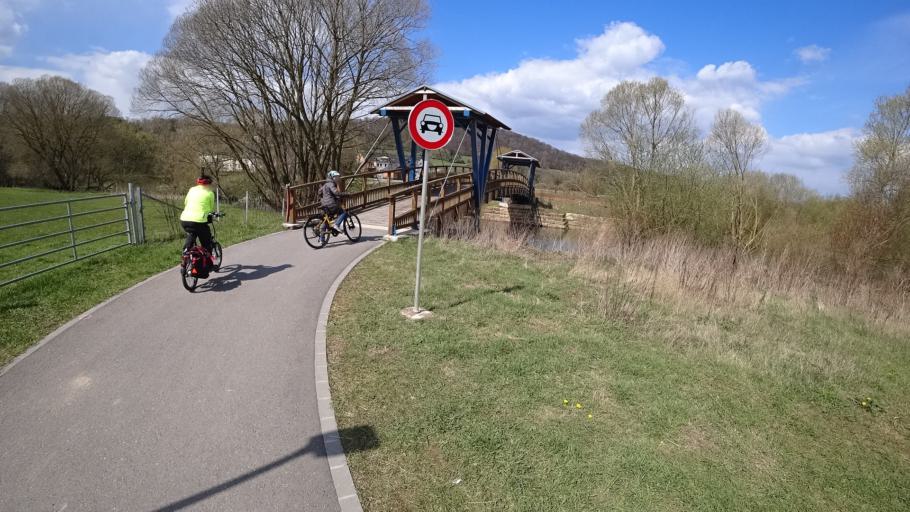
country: LU
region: Luxembourg
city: Colmar
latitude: 49.8175
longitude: 6.0960
